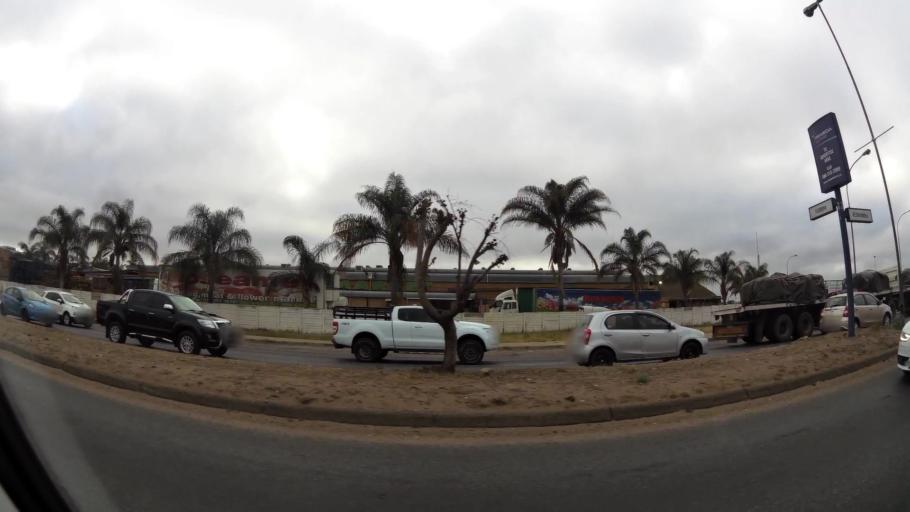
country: ZA
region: Limpopo
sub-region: Capricorn District Municipality
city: Polokwane
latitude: -23.8989
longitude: 29.4393
